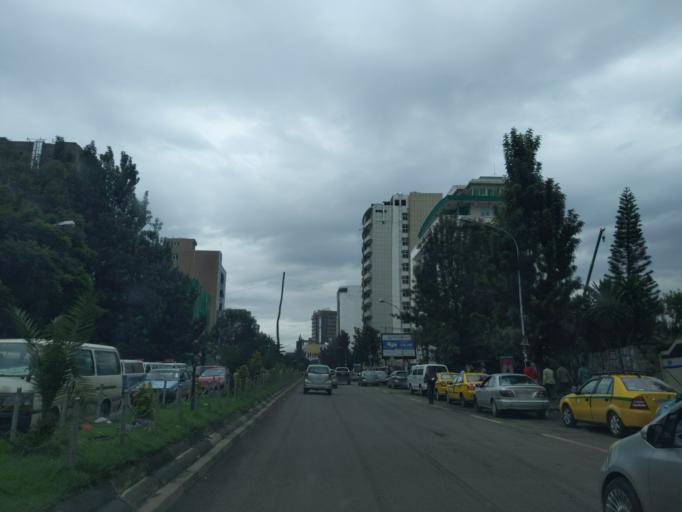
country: ET
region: Adis Abeba
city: Addis Ababa
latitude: 8.9910
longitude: 38.7927
